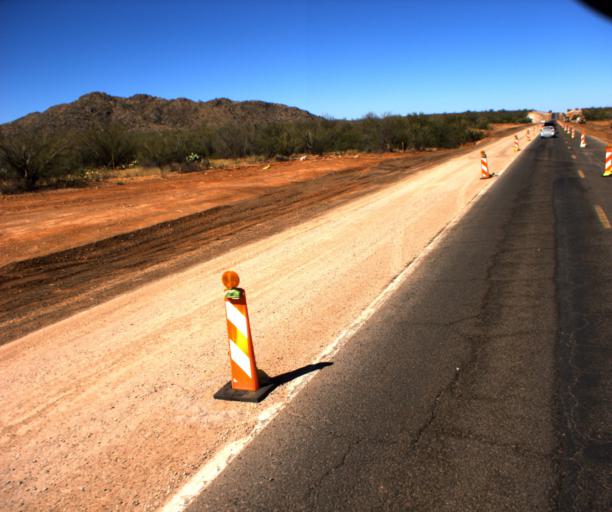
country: US
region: Arizona
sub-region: Pima County
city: Sells
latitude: 32.0042
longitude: -111.6819
